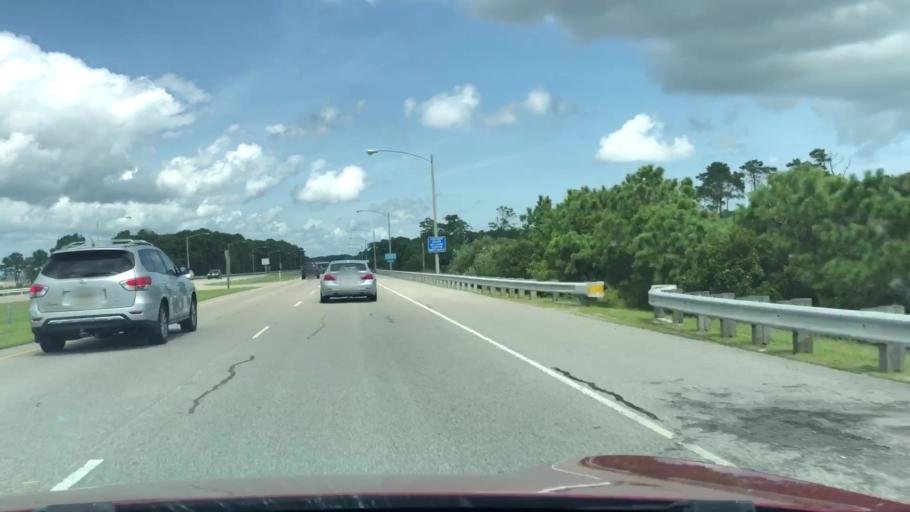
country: US
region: Virginia
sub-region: Northampton County
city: Cape Charles
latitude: 37.1211
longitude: -75.9679
